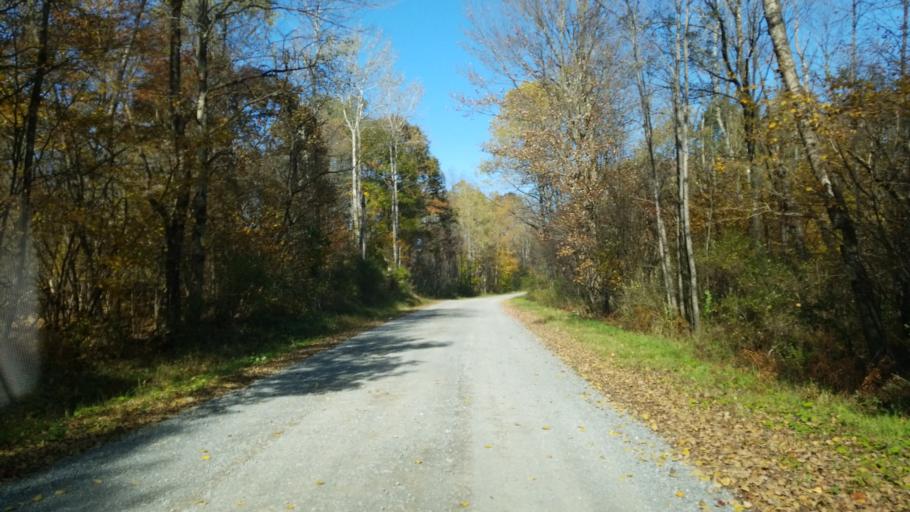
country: US
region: Pennsylvania
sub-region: Jefferson County
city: Falls Creek
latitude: 41.1775
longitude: -78.7838
